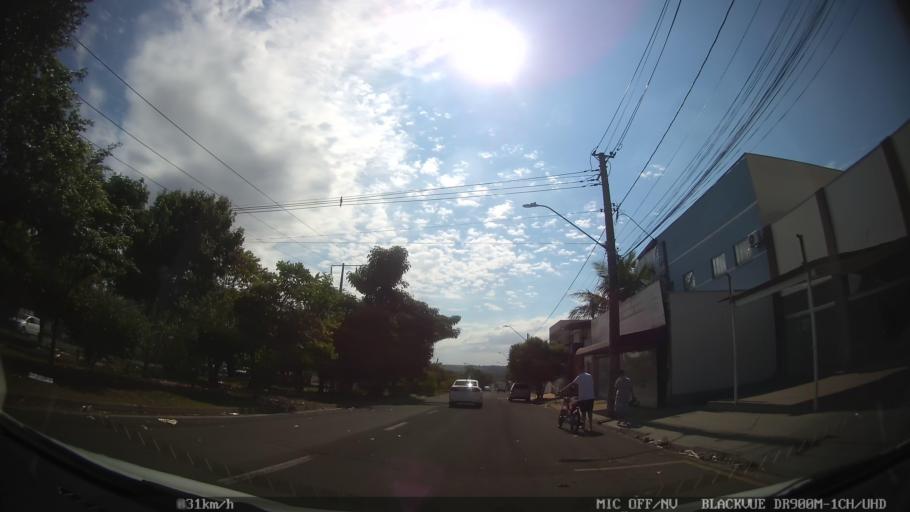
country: BR
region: Sao Paulo
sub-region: Americana
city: Americana
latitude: -22.7179
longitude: -47.3201
